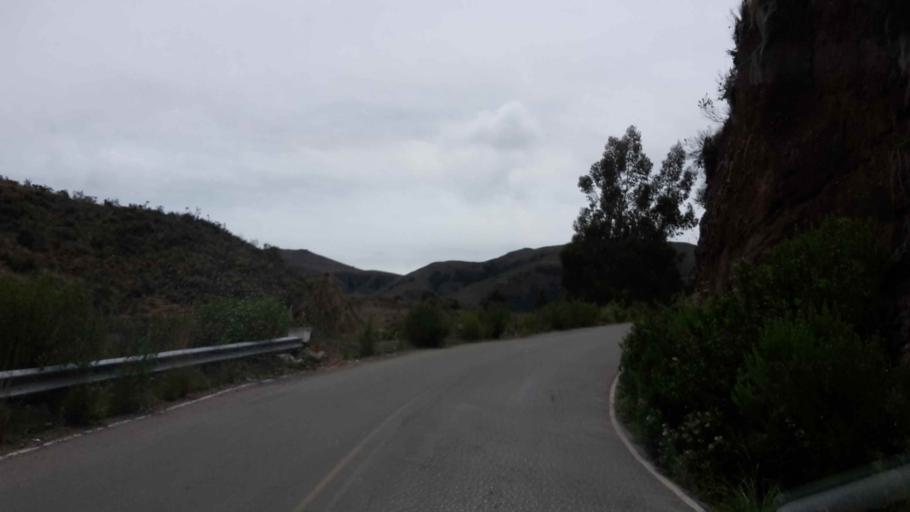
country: BO
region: Cochabamba
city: Colomi
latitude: -17.4018
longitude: -65.8082
